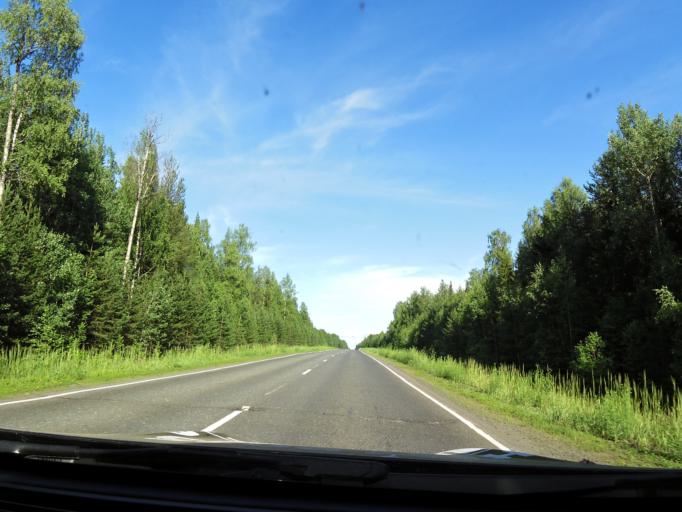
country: RU
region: Kirov
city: Chernaya Kholunitsa
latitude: 58.8854
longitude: 51.3973
